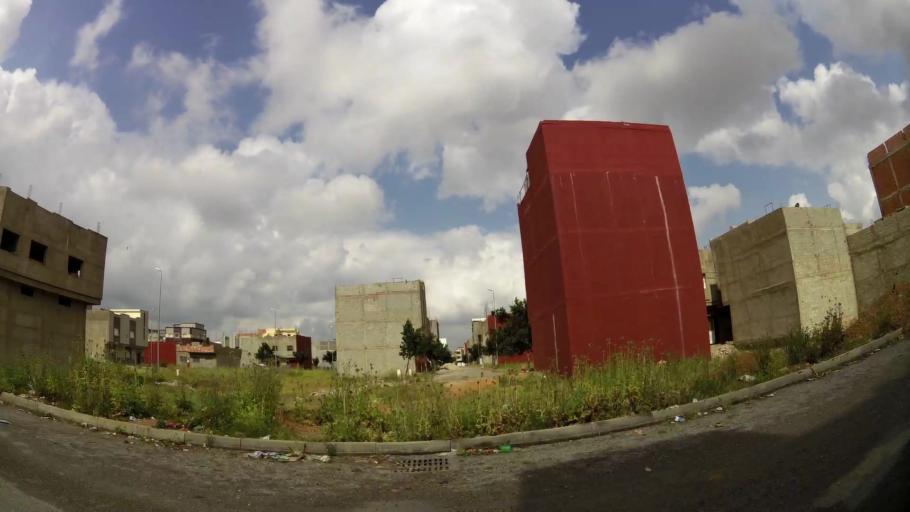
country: MA
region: Rabat-Sale-Zemmour-Zaer
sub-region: Khemisset
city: Tiflet
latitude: 33.8977
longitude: -6.3322
